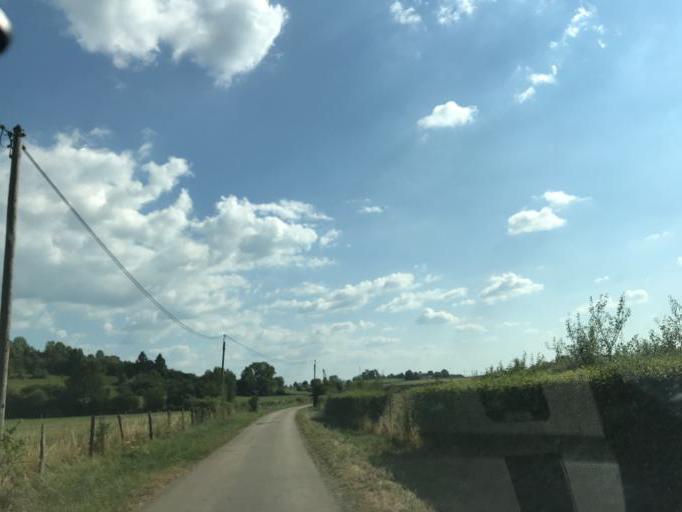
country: FR
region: Franche-Comte
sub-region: Departement du Jura
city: Clairvaux-les-Lacs
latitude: 46.5890
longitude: 5.7300
